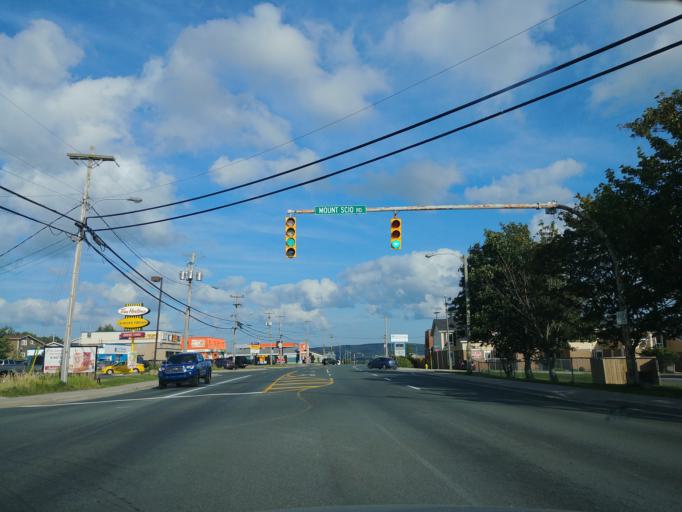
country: CA
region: Newfoundland and Labrador
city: Mount Pearl
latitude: 47.5645
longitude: -52.7636
